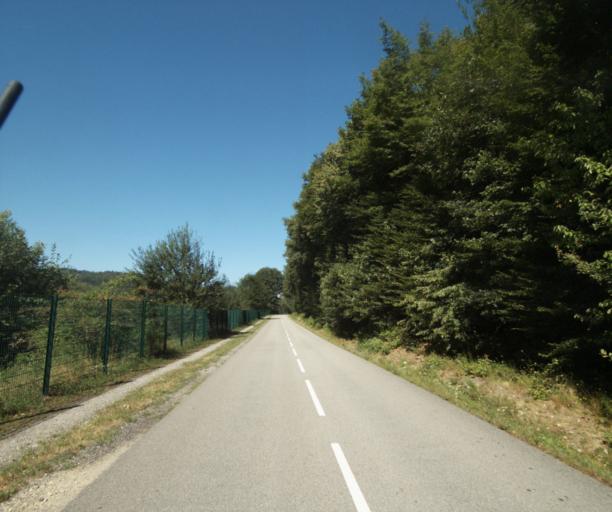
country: FR
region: Lorraine
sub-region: Departement des Vosges
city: Arches
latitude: 48.1438
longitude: 6.4836
